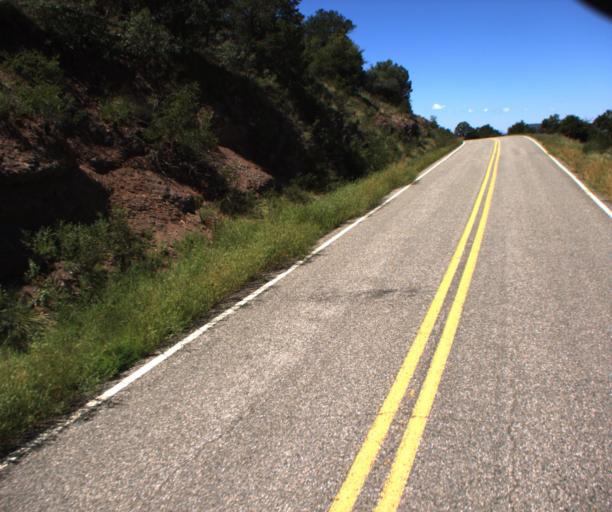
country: US
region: Arizona
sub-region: Greenlee County
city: Morenci
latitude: 33.3672
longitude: -109.3305
